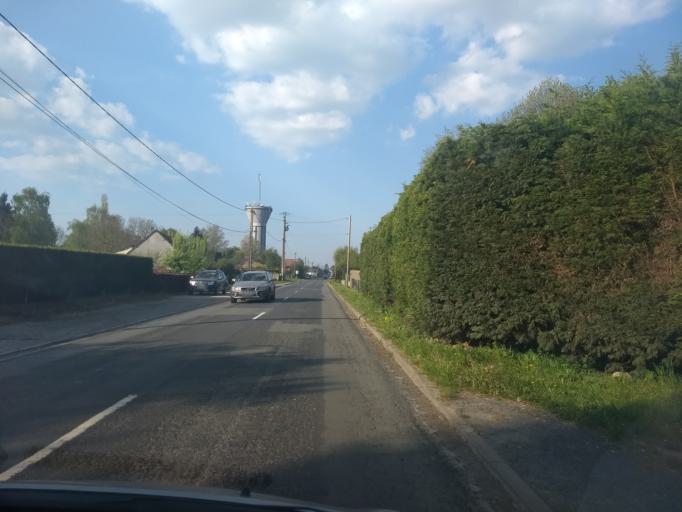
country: FR
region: Picardie
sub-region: Departement de la Somme
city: Albert
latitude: 50.0838
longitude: 2.6089
